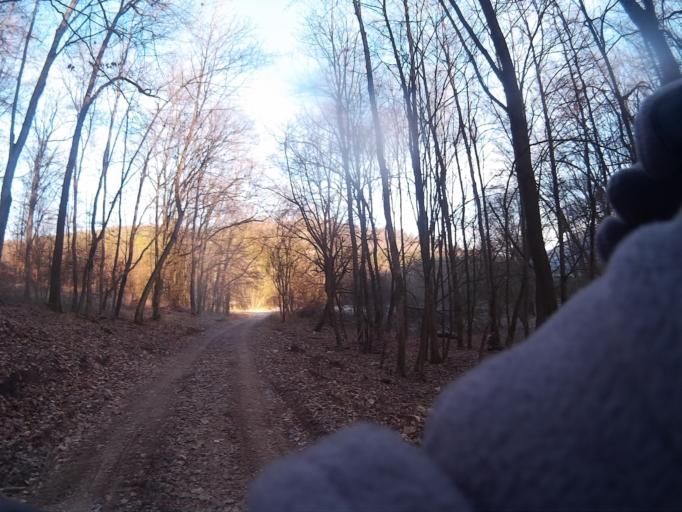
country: HU
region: Borsod-Abauj-Zemplen
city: Rudabanya
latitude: 48.5298
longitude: 20.6256
